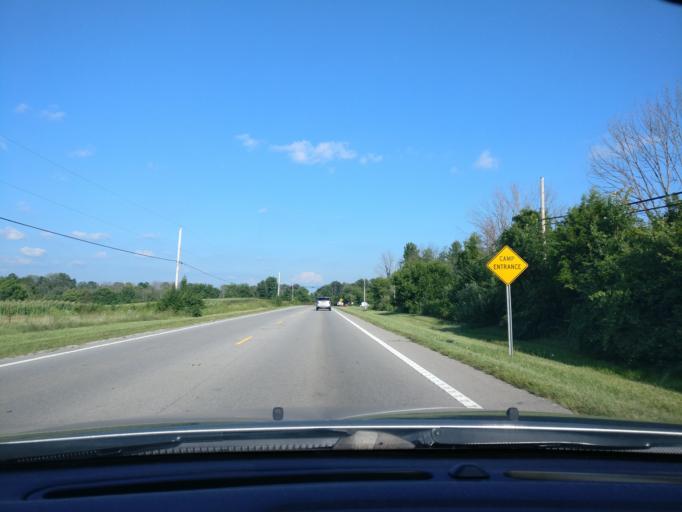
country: US
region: Ohio
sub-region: Warren County
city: Waynesville
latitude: 39.5423
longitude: -84.1087
